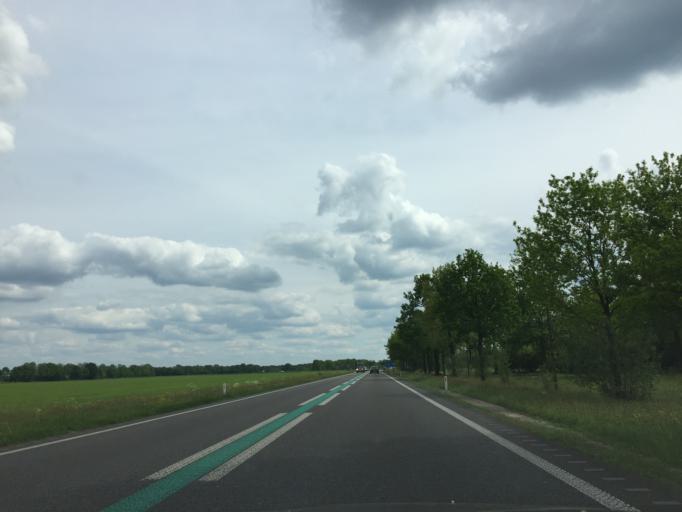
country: NL
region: Drenthe
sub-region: Gemeente Borger-Odoorn
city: Borger
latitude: 52.9813
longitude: 6.7714
